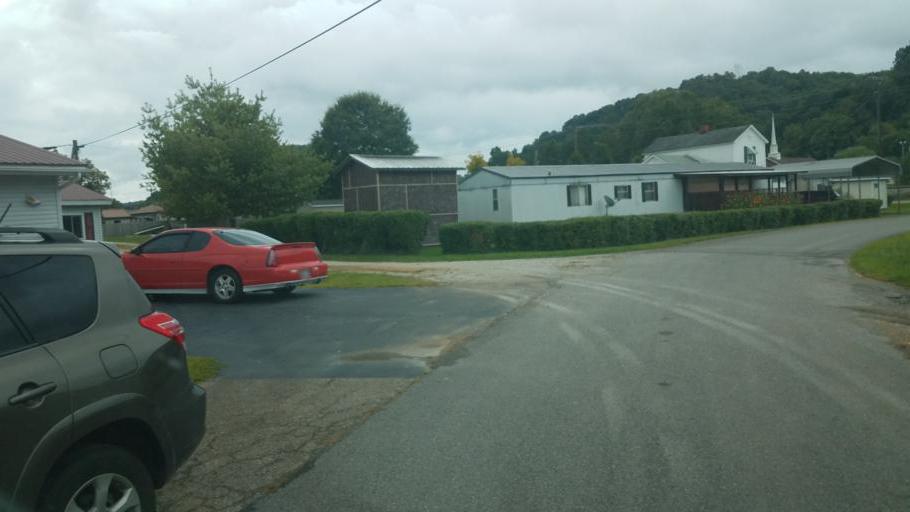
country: US
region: Kentucky
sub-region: Greenup County
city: South Shore
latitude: 38.7215
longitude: -82.9690
